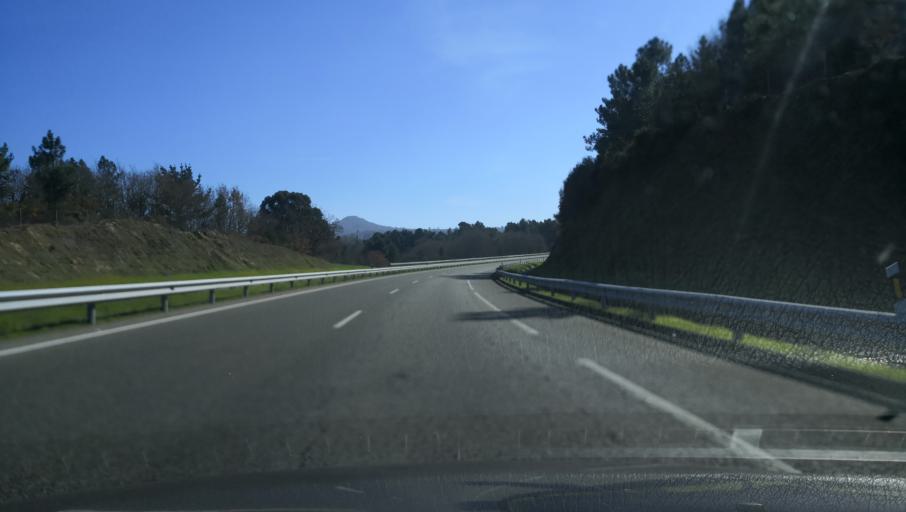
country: ES
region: Galicia
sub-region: Provincia de Ourense
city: Taboadela
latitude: 42.2347
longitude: -7.8491
